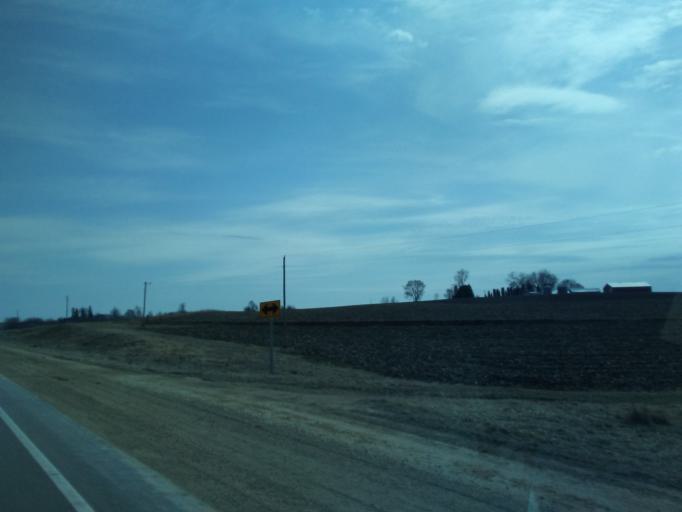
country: US
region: Iowa
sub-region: Winneshiek County
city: Decorah
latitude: 43.3901
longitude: -91.8302
